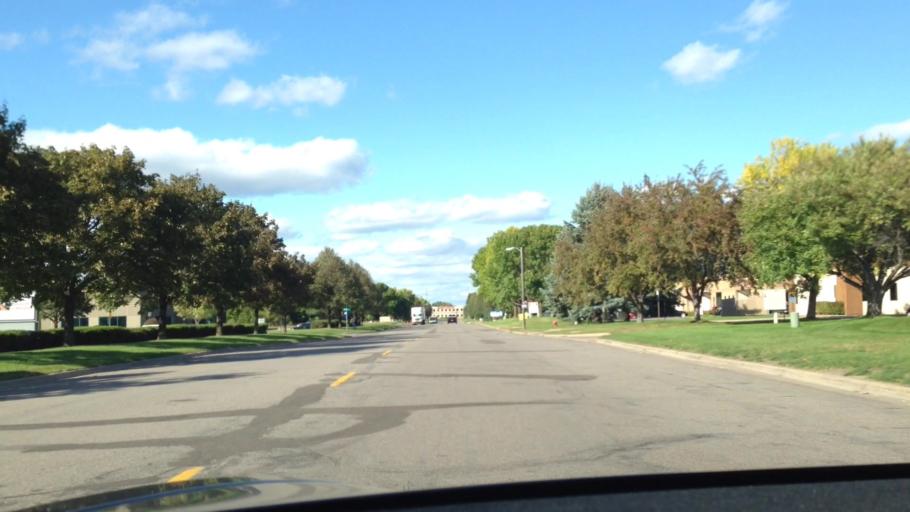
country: US
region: Minnesota
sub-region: Hennepin County
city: Osseo
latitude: 45.1108
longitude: -93.3869
